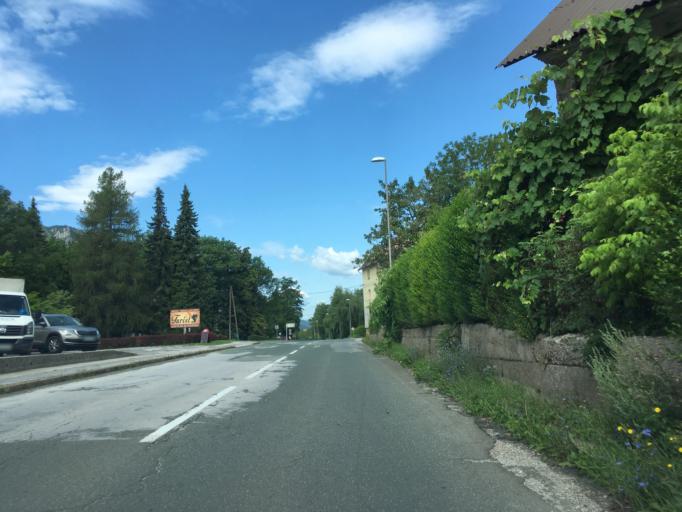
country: SI
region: Jesenice
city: Slovenski Javornik
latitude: 46.4265
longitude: 14.0897
